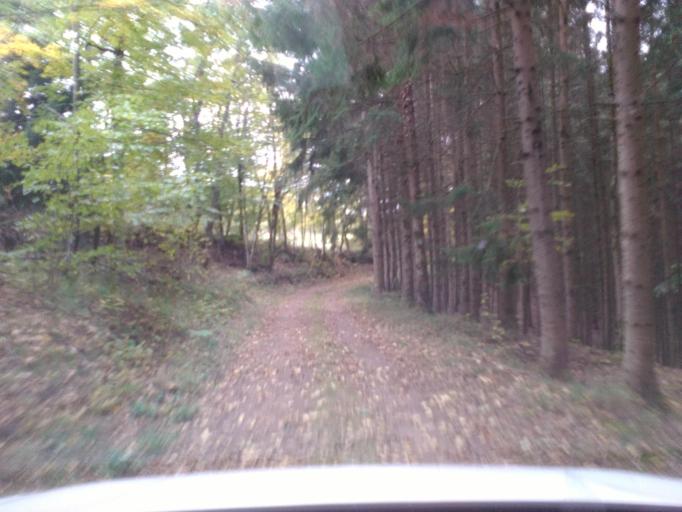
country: FR
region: Lorraine
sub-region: Departement des Vosges
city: Senones
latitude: 48.3335
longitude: 7.0088
